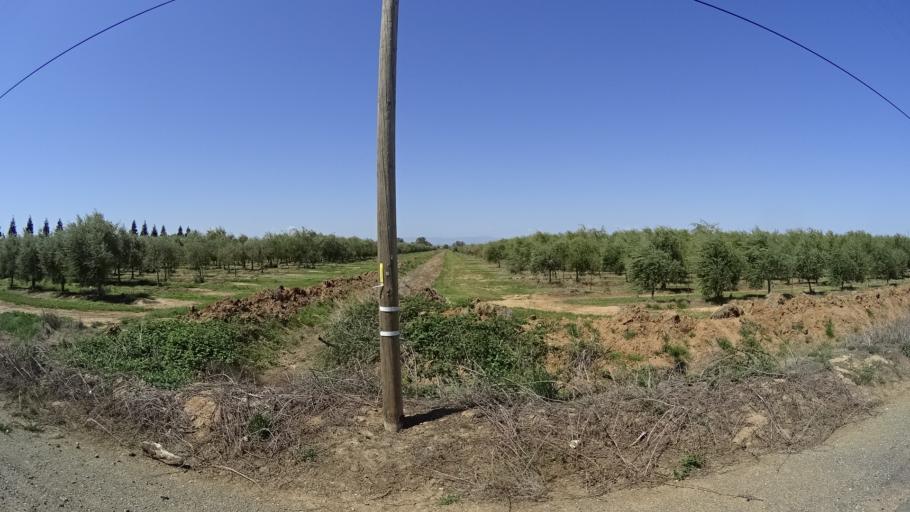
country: US
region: California
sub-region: Glenn County
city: Orland
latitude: 39.7880
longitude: -122.1690
